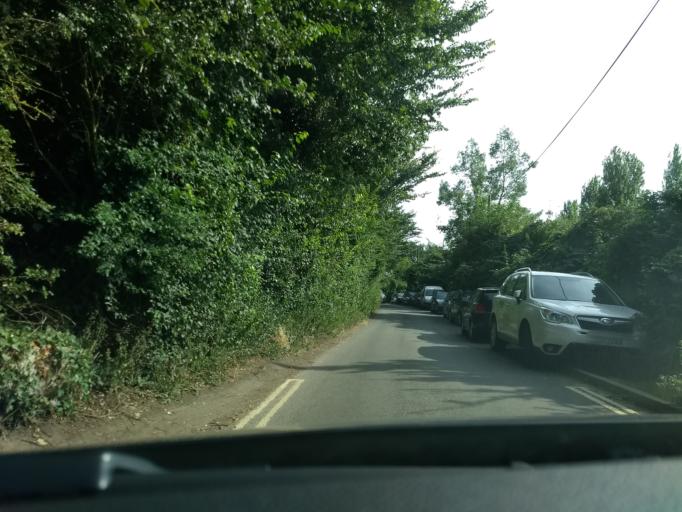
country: GB
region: England
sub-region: Suffolk
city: Shotley Gate
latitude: 51.9945
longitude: 1.2122
